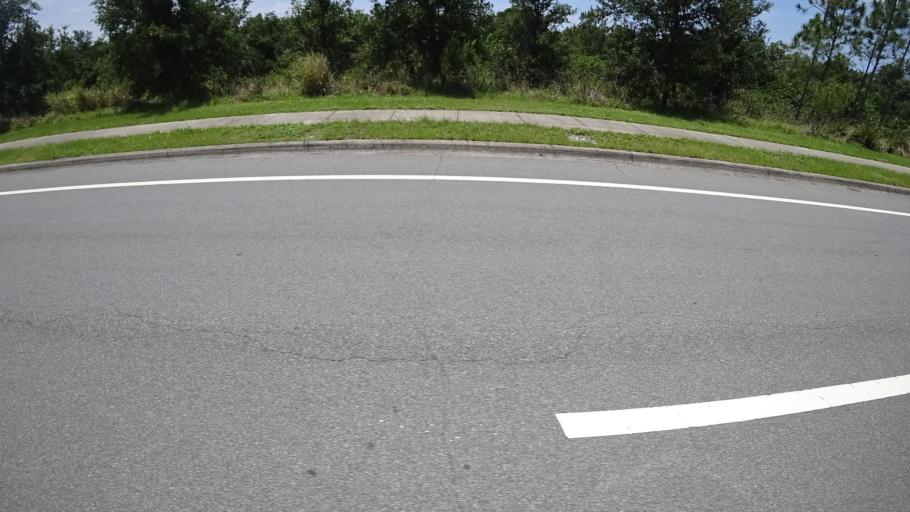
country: US
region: Florida
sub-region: Sarasota County
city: Desoto Lakes
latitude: 27.4256
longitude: -82.4956
